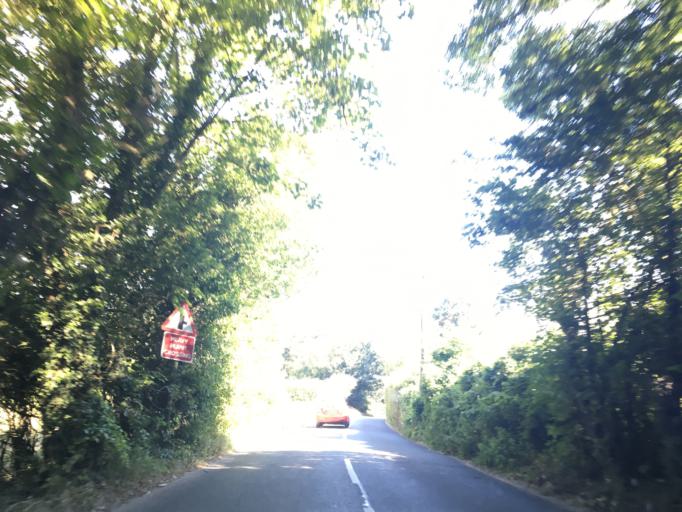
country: GB
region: England
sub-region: Isle of Wight
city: Newport
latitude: 50.6862
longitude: -1.3086
